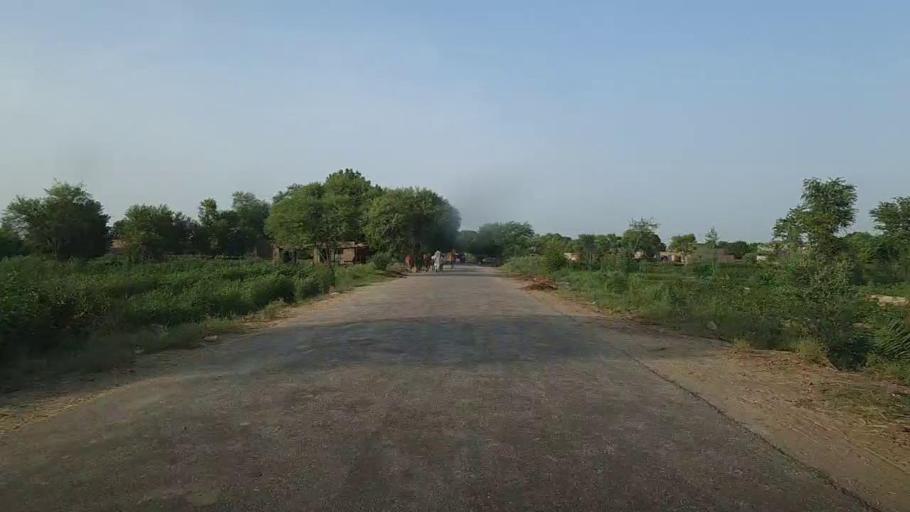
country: PK
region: Sindh
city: Ubauro
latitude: 28.1311
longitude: 69.8336
